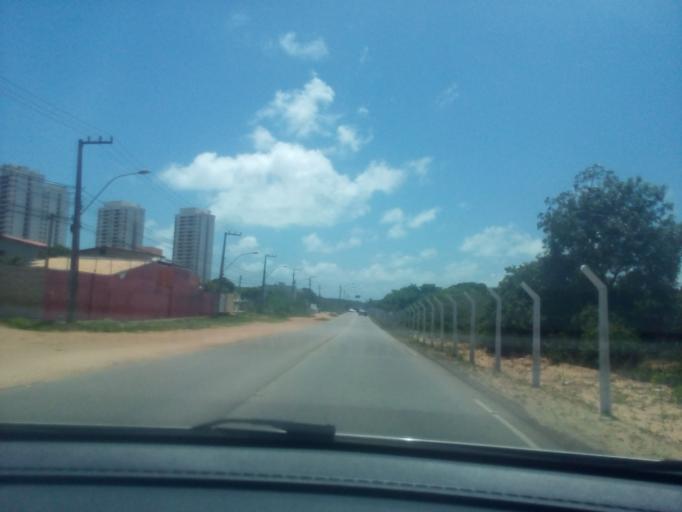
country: BR
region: Rio Grande do Norte
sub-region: Parnamirim
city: Parnamirim
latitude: -5.8921
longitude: -35.1819
